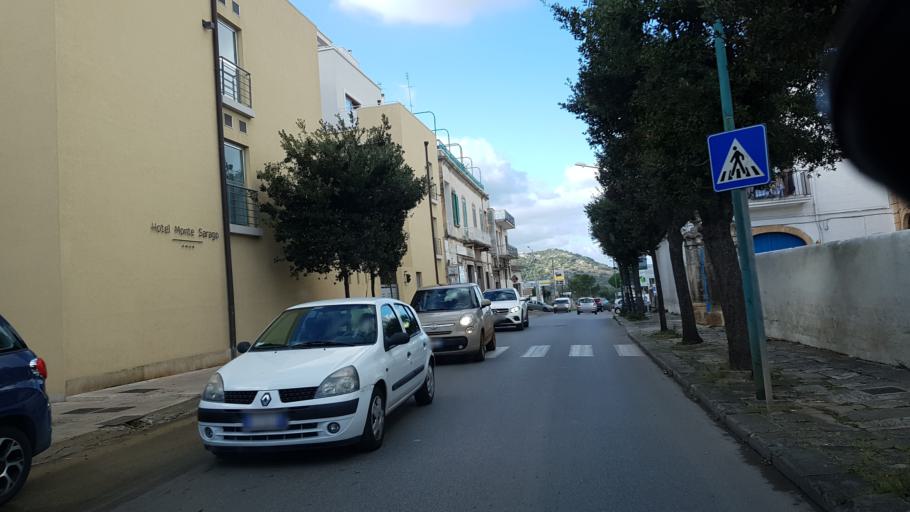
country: IT
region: Apulia
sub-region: Provincia di Brindisi
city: Ostuni
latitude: 40.7321
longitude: 17.5697
